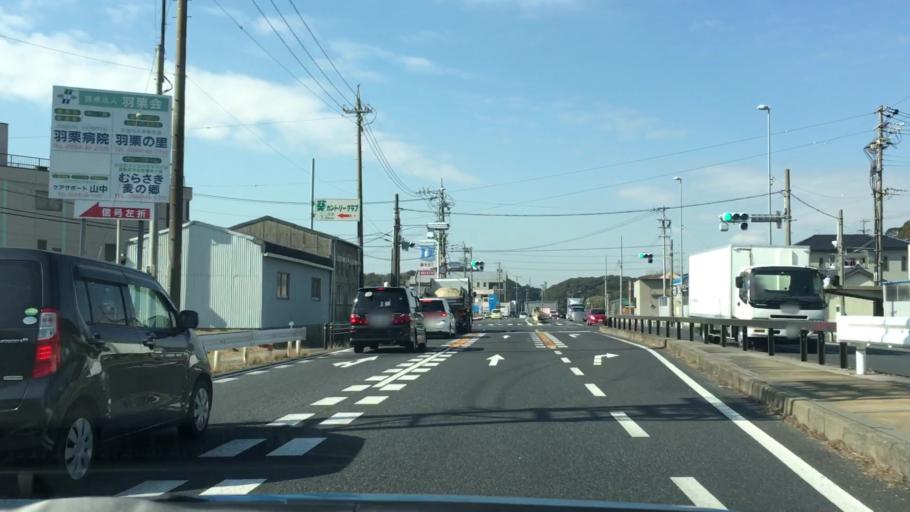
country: JP
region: Aichi
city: Gamagori
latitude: 34.8989
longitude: 137.2424
